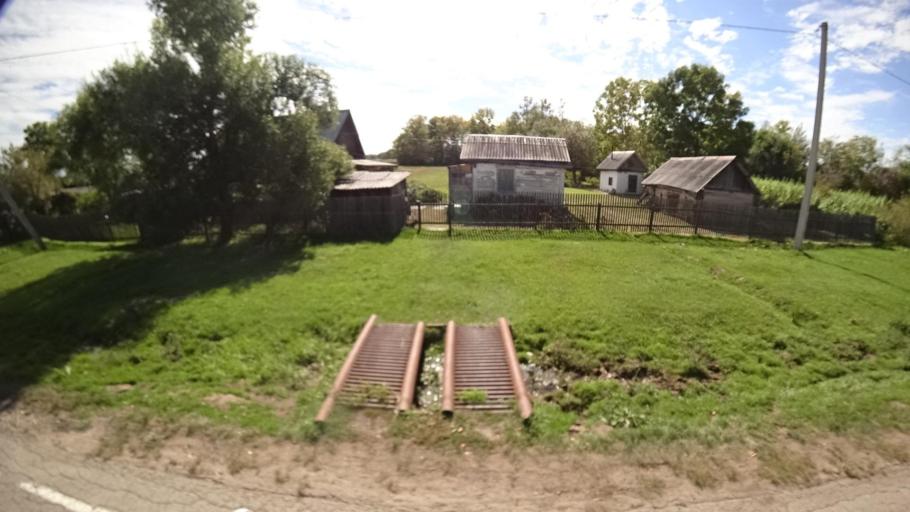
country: RU
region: Primorskiy
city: Yakovlevka
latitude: 44.4275
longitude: 133.5731
